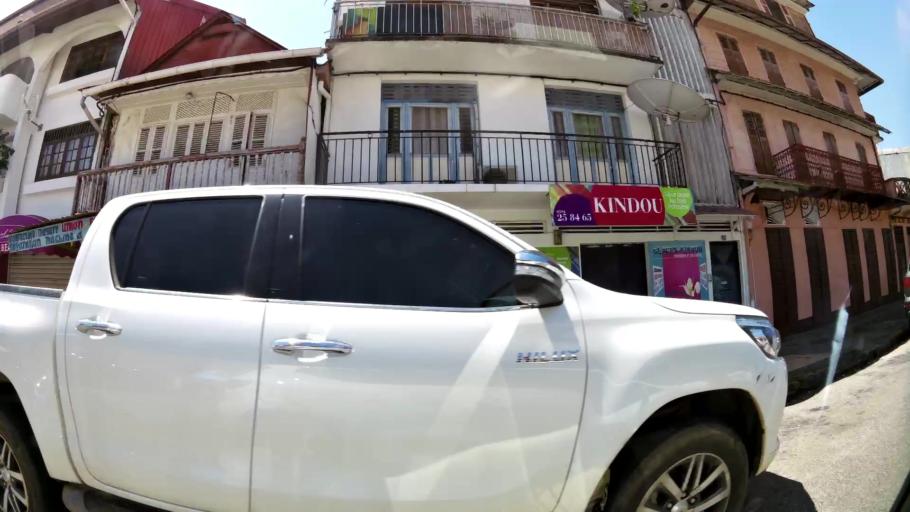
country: GF
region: Guyane
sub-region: Guyane
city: Cayenne
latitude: 4.9405
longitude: -52.3302
